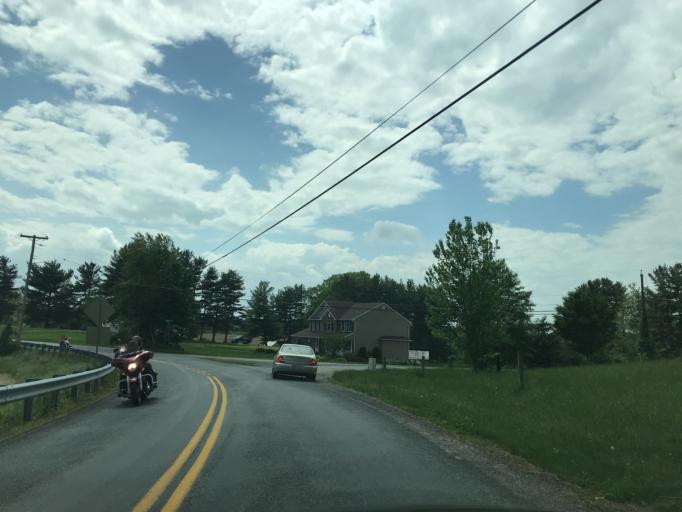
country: US
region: Maryland
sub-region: Harford County
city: Bel Air North
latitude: 39.6135
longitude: -76.3572
